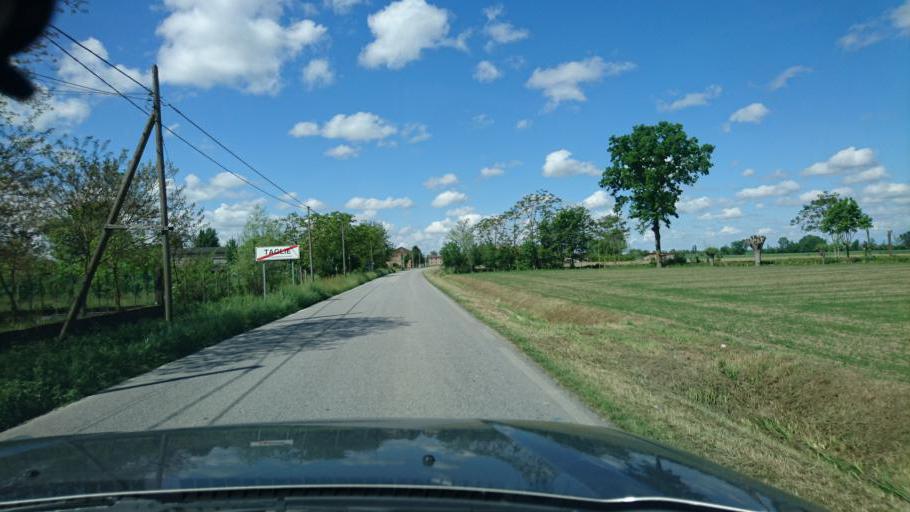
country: IT
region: Veneto
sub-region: Provincia di Padova
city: Santa Margherita d'Adige
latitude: 45.1919
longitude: 11.5538
